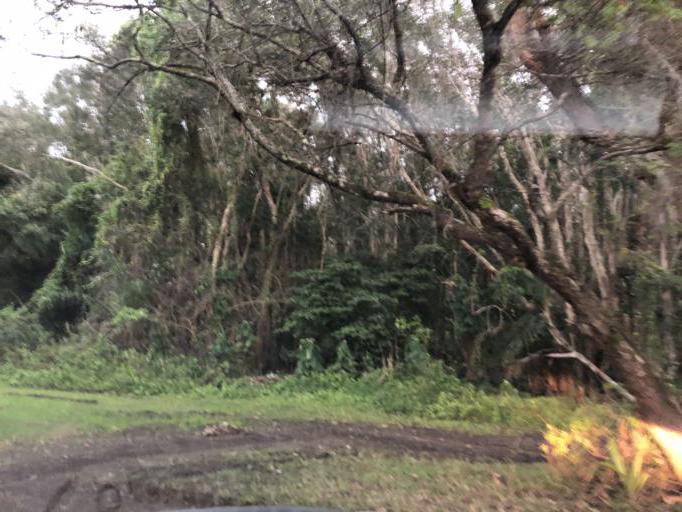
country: AU
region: New South Wales
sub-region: Coffs Harbour
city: Coffs Harbour
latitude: -30.3118
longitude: 153.1332
